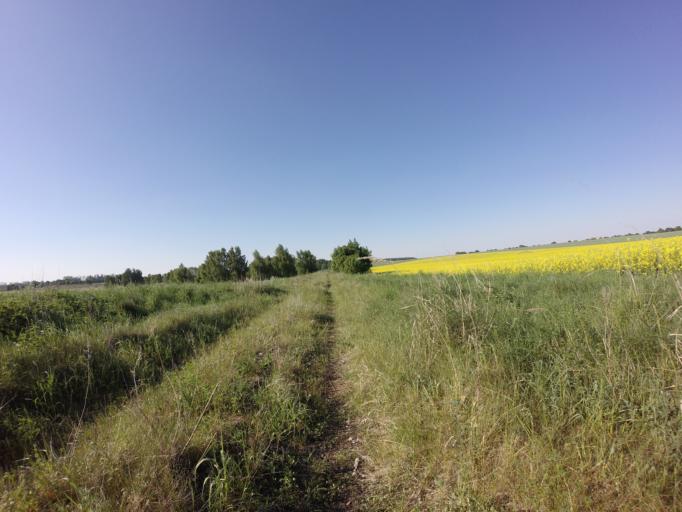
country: PL
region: West Pomeranian Voivodeship
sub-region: Powiat choszczenski
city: Choszczno
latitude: 53.1410
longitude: 15.3694
